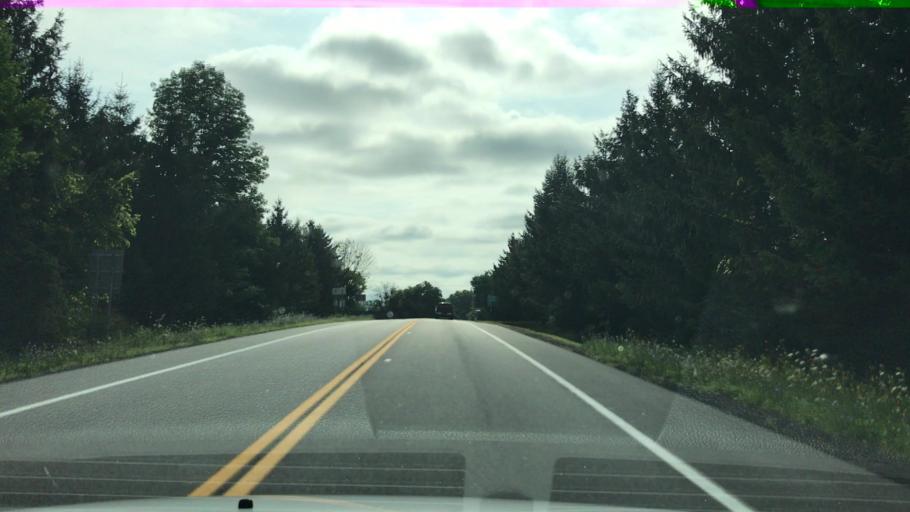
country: US
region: New York
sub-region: Erie County
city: Alden
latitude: 42.8499
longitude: -78.4879
